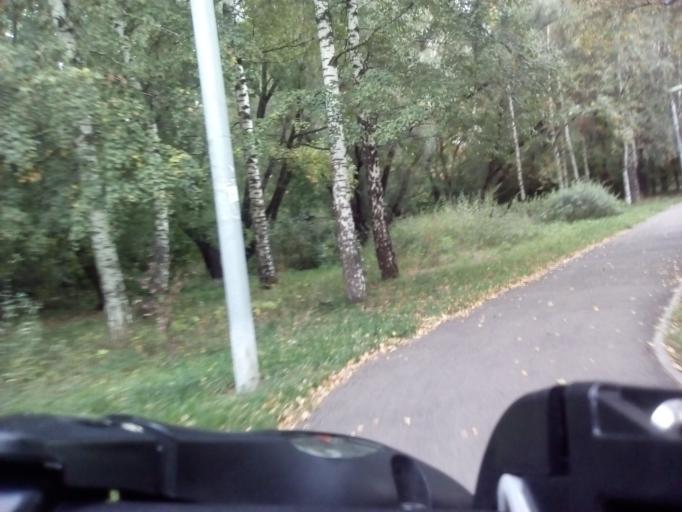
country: RU
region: Moscow
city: Leonovo
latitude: 55.8378
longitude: 37.6505
